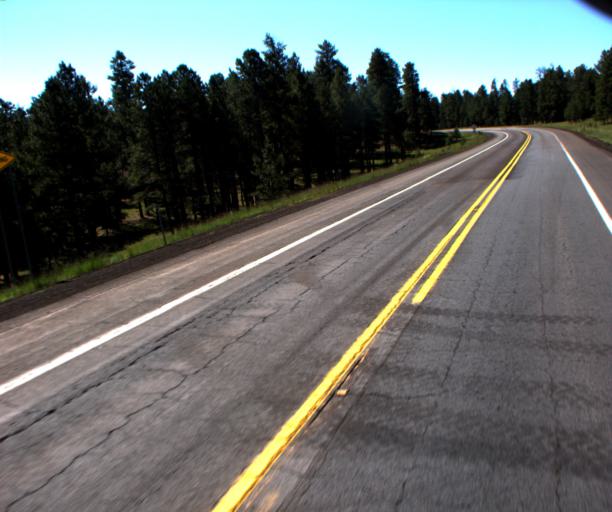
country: US
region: New Mexico
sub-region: Catron County
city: Reserve
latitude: 33.8182
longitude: -109.0738
